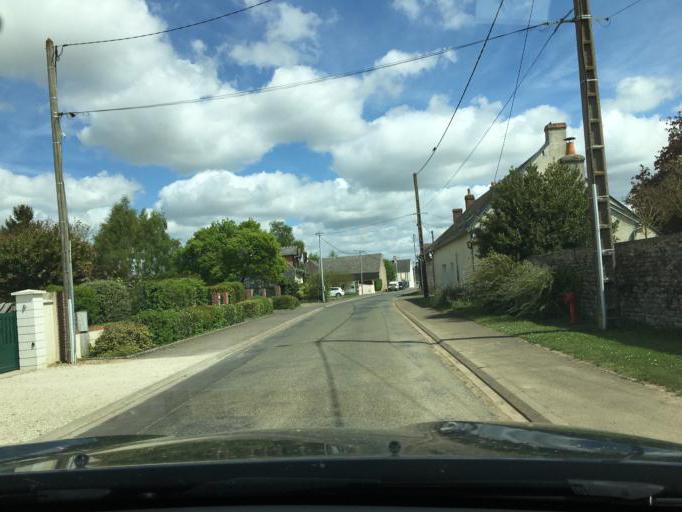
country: FR
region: Centre
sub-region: Departement du Loiret
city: Bricy
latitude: 48.0522
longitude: 1.7853
